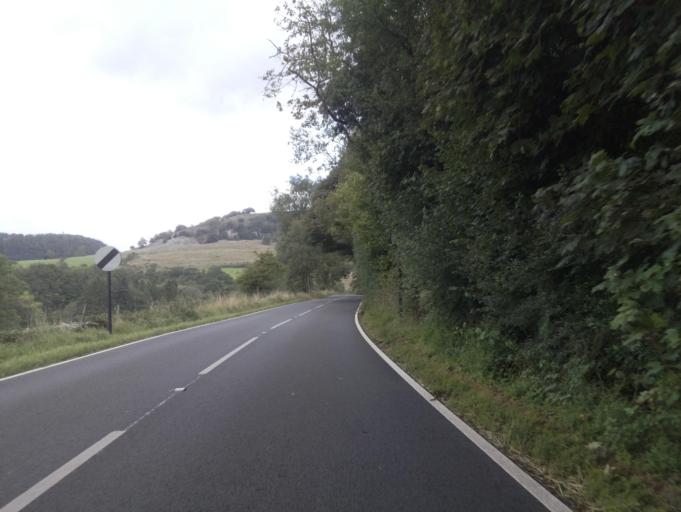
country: GB
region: England
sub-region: North Yorkshire
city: Leyburn
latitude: 54.4018
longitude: -1.8235
